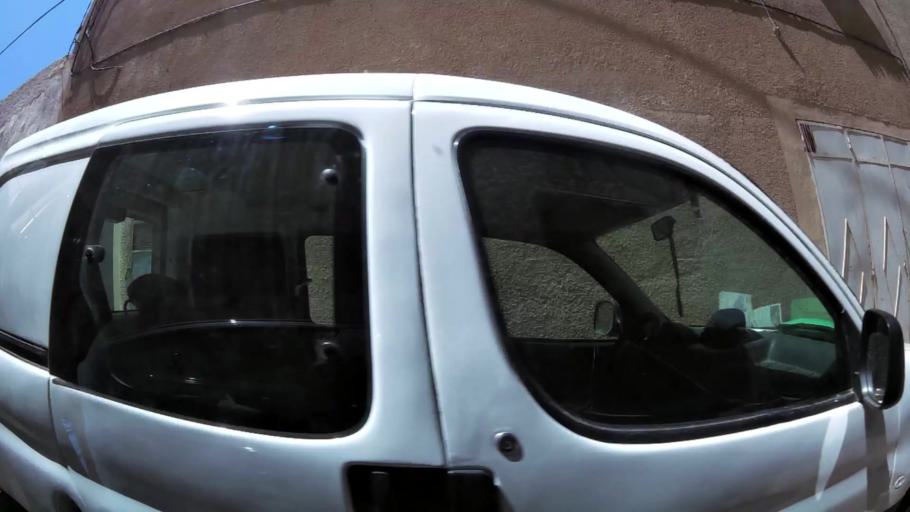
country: MA
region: Oriental
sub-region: Oujda-Angad
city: Oujda
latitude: 34.6790
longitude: -1.9547
